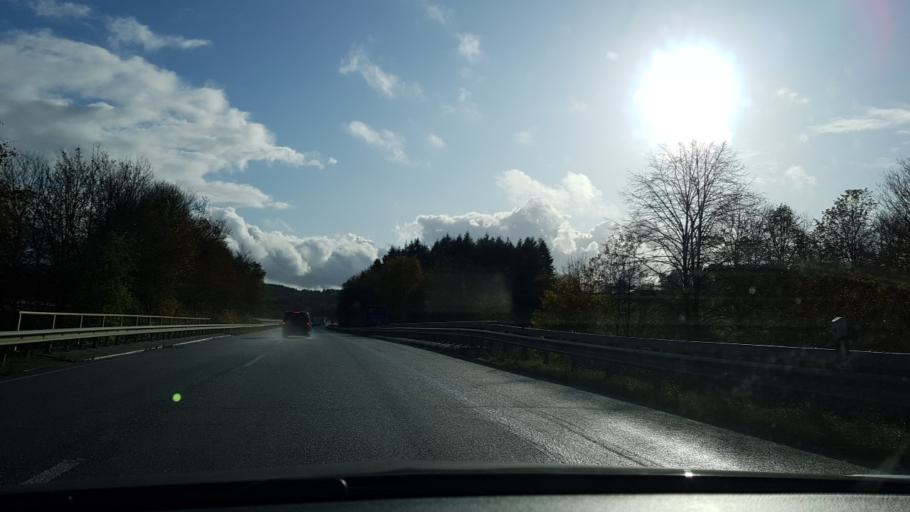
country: DE
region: Rheinland-Pfalz
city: Mehren
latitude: 50.1782
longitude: 6.8957
